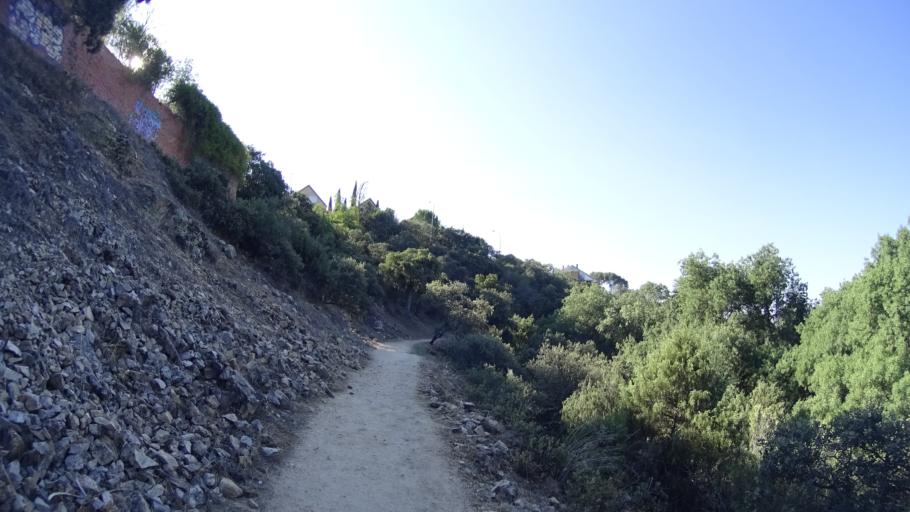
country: ES
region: Madrid
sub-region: Provincia de Madrid
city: Las Matas
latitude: 40.5809
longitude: -3.8951
